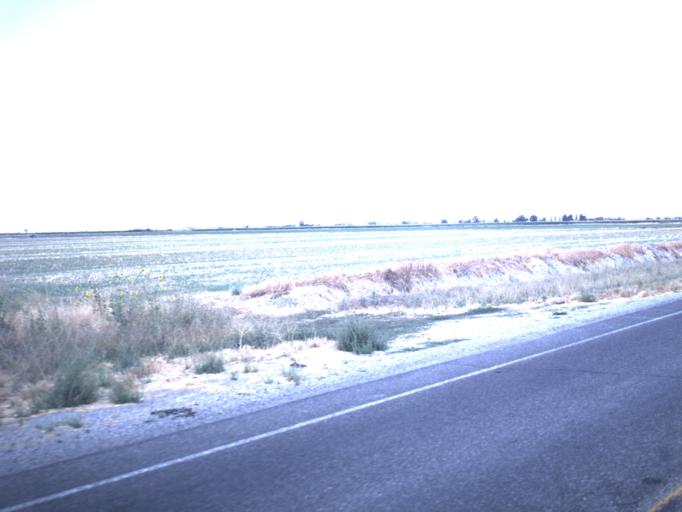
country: US
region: Utah
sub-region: Box Elder County
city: Honeyville
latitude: 41.5896
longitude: -112.1298
